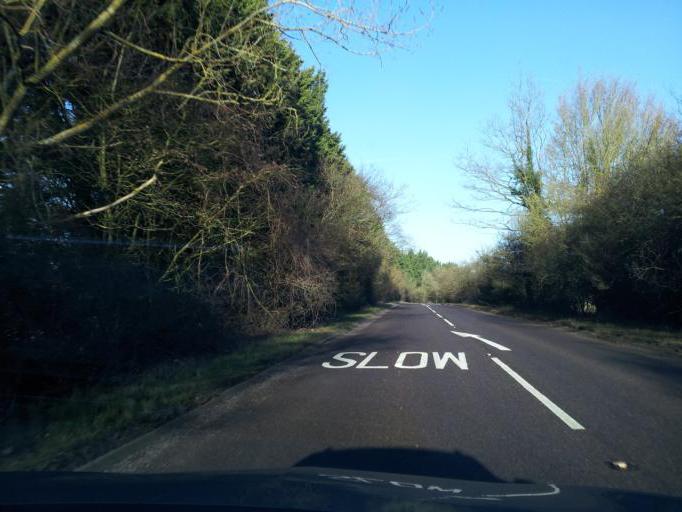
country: GB
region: England
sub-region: Suffolk
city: Lavenham
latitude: 52.1331
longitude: 0.7532
